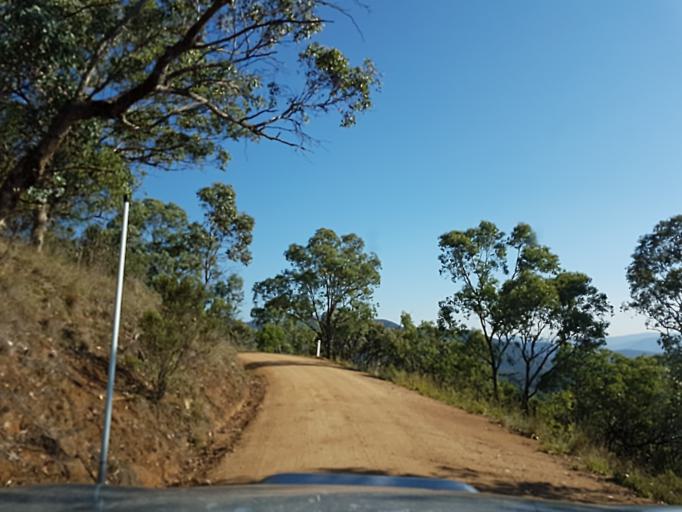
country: AU
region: New South Wales
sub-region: Snowy River
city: Jindabyne
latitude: -36.9450
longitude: 148.3478
